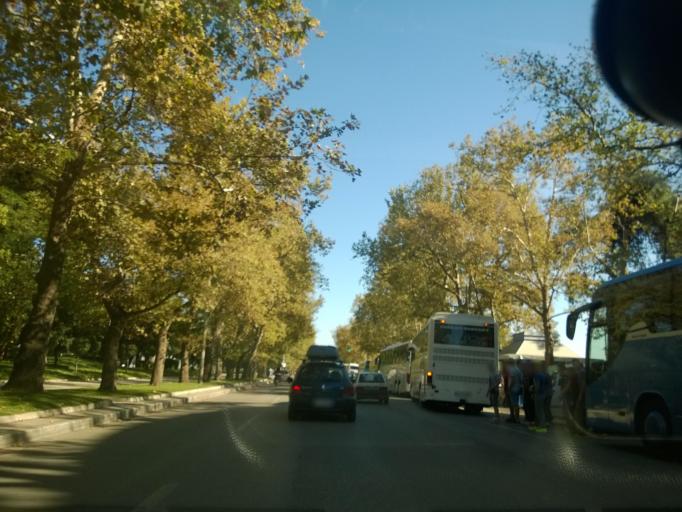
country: GR
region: Central Macedonia
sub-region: Nomos Thessalonikis
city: Agios Pavlos
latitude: 40.6254
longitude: 22.9502
